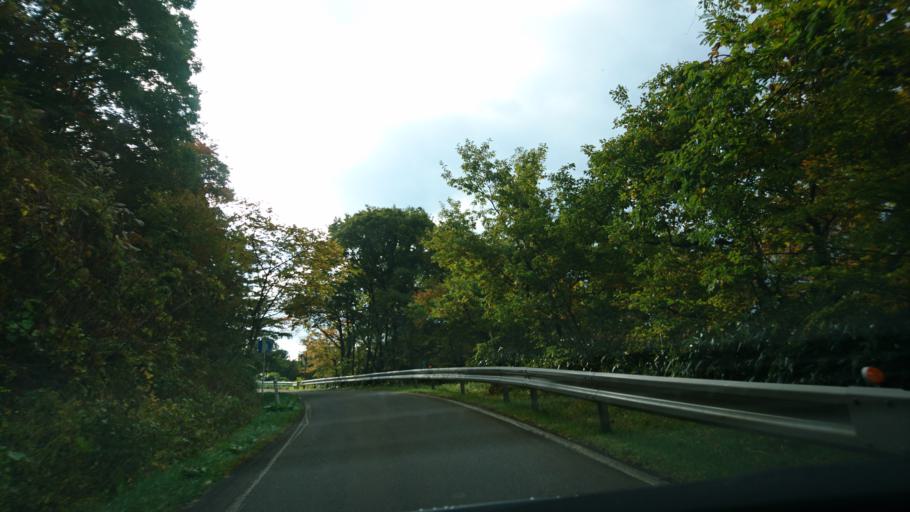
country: JP
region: Iwate
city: Mizusawa
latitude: 39.0995
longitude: 140.9725
